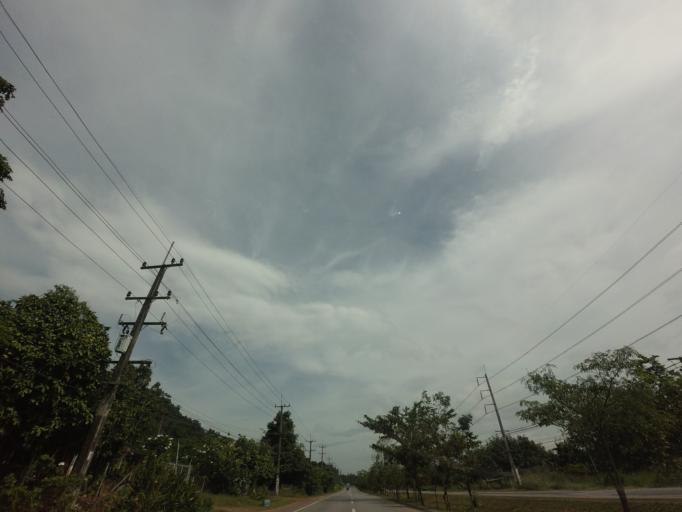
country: TH
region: Rayong
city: Klaeng
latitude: 12.6964
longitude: 101.5394
